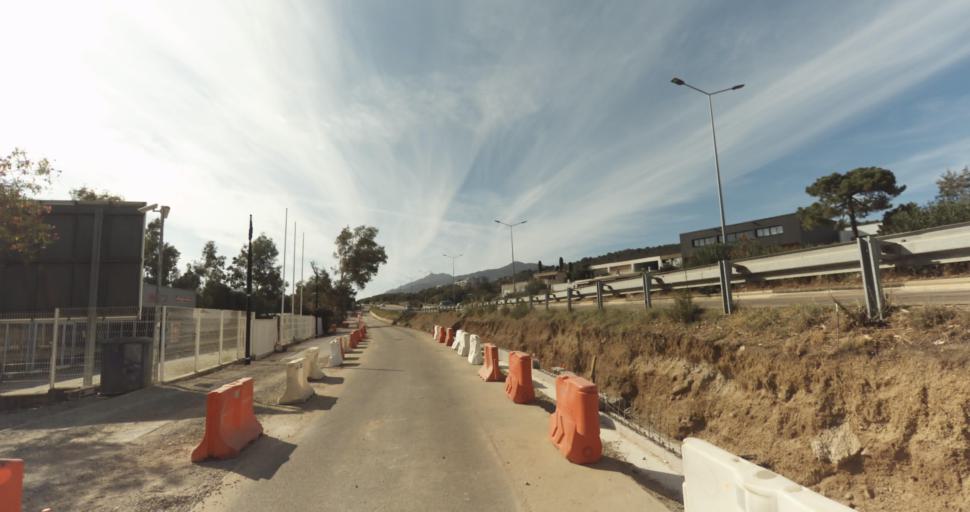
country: FR
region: Corsica
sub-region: Departement de la Corse-du-Sud
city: Ajaccio
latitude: 41.9283
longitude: 8.7733
